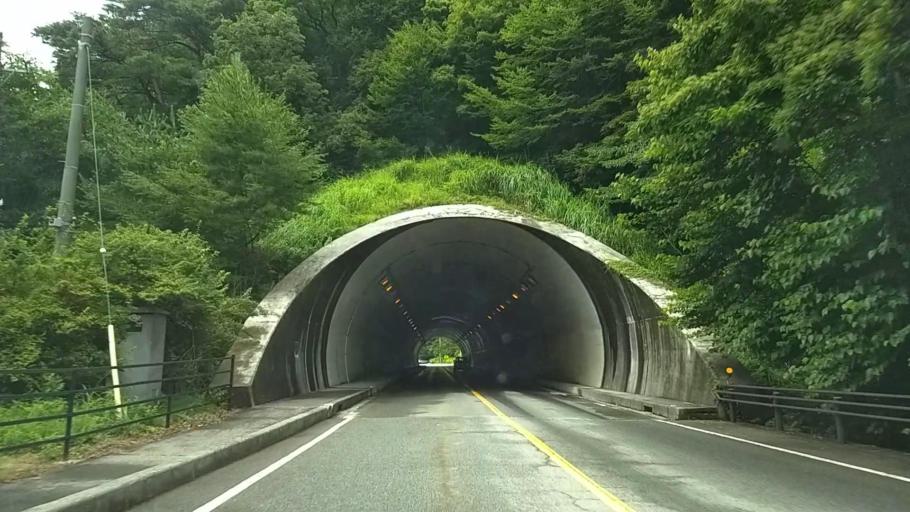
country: JP
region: Yamanashi
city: Fujikawaguchiko
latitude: 35.4717
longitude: 138.5968
